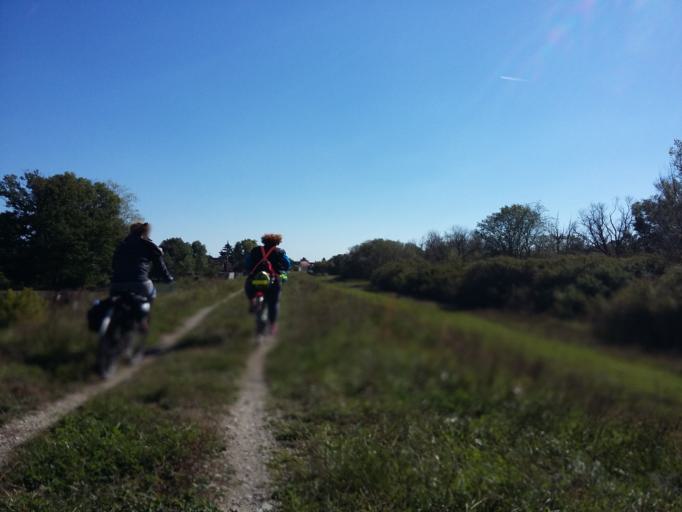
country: AT
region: Lower Austria
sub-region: Politischer Bezirk Ganserndorf
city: Marchegg
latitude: 48.3296
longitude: 16.9056
